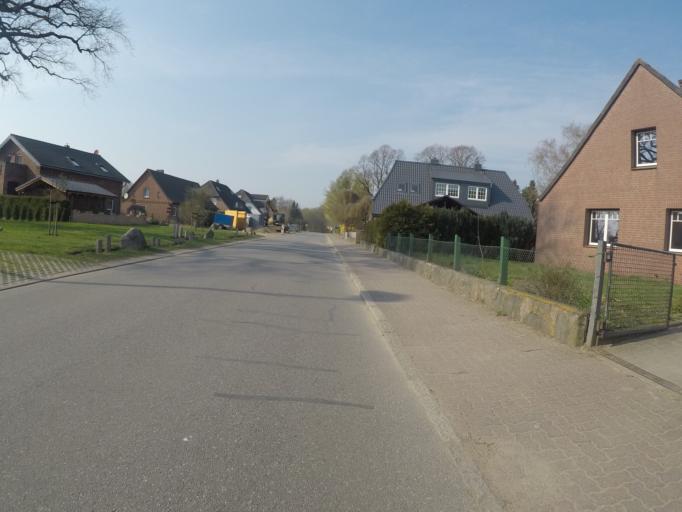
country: DE
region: Schleswig-Holstein
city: Gross Niendorf
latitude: 53.8488
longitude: 10.2441
